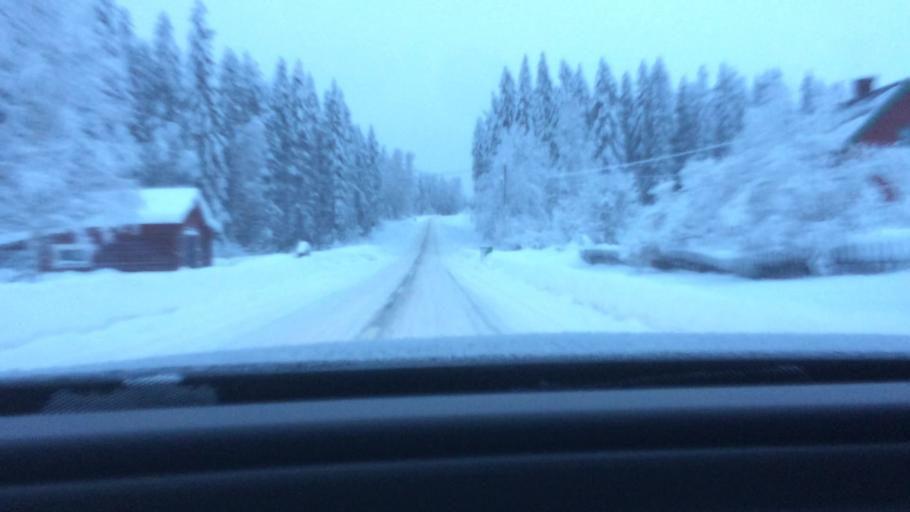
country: SE
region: Gaevleborg
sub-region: Ljusdals Kommun
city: Farila
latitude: 61.7709
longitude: 15.1671
